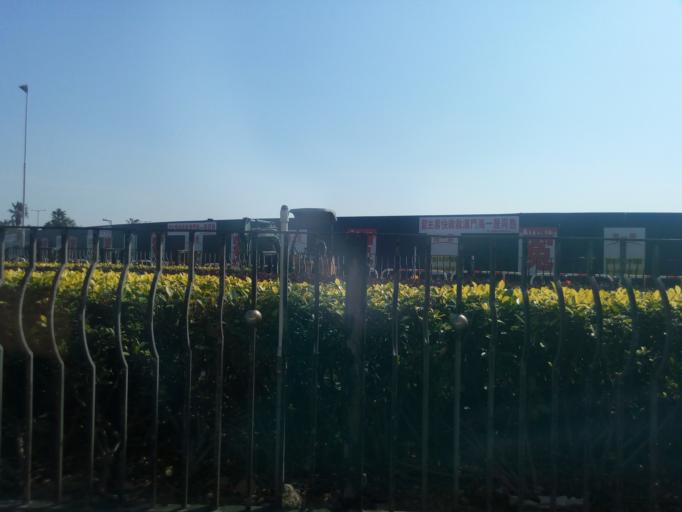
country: MO
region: Macau
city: Macau
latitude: 22.2110
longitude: 113.5588
